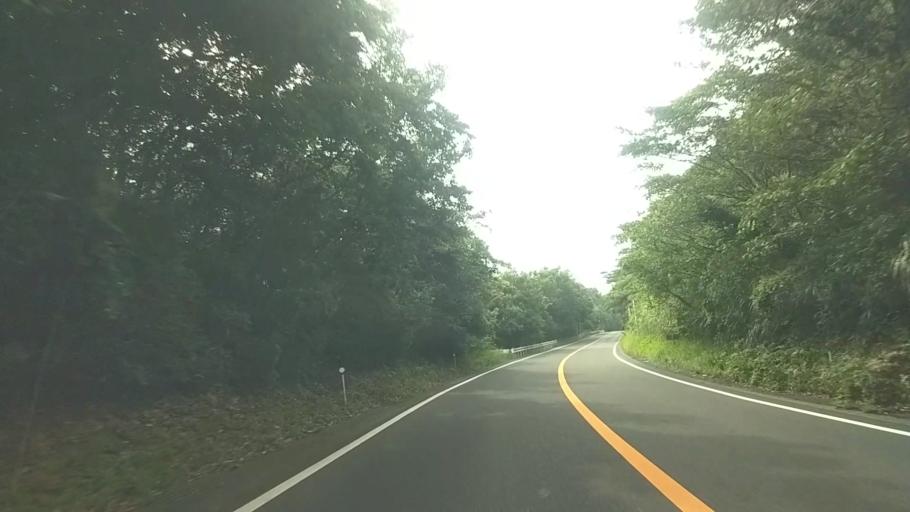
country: JP
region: Chiba
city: Kimitsu
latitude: 35.2338
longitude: 140.0126
